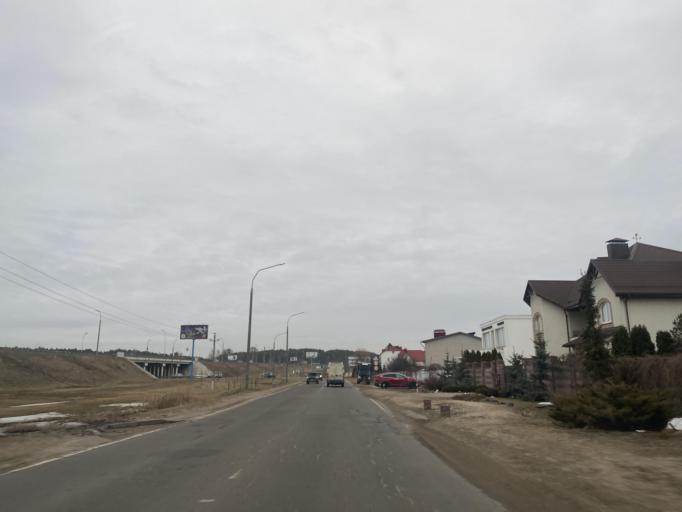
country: BY
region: Minsk
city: Bal'shavik
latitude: 53.9702
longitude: 27.5916
